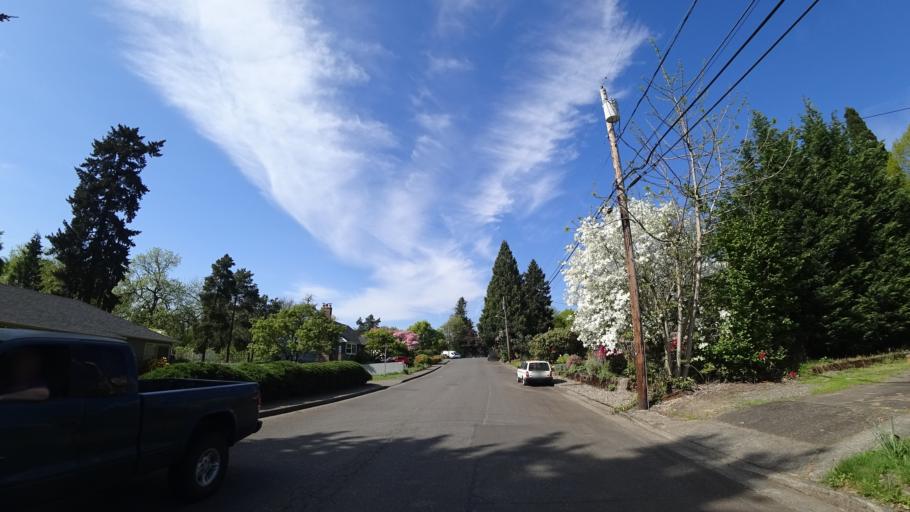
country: US
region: Oregon
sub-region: Clackamas County
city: Milwaukie
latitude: 45.4611
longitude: -122.6263
